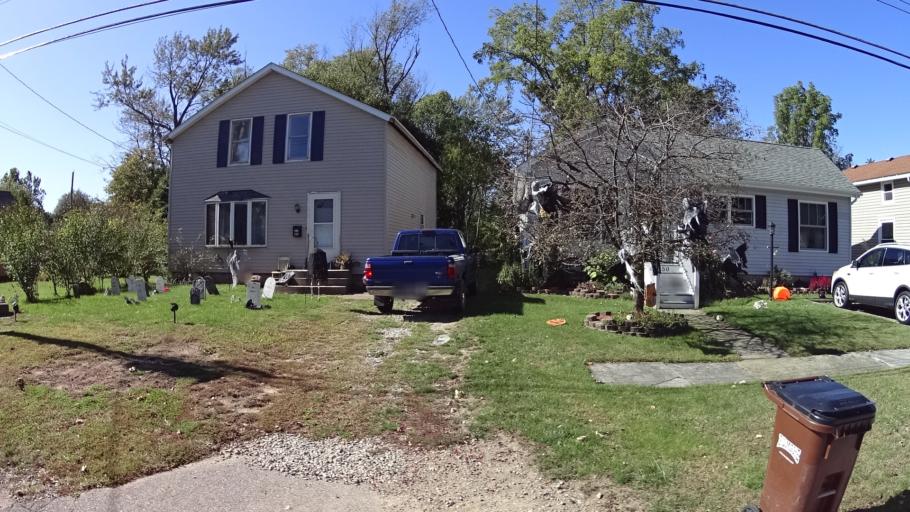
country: US
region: Ohio
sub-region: Lorain County
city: Amherst
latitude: 41.3976
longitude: -82.2141
